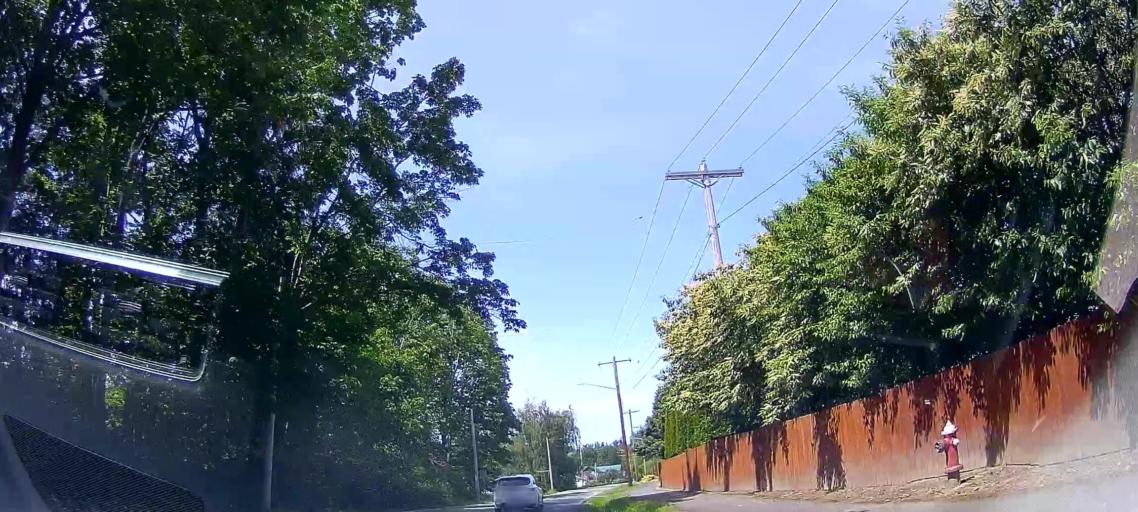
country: US
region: Washington
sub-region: Snohomish County
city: Stanwood
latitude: 48.2364
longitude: -122.3436
